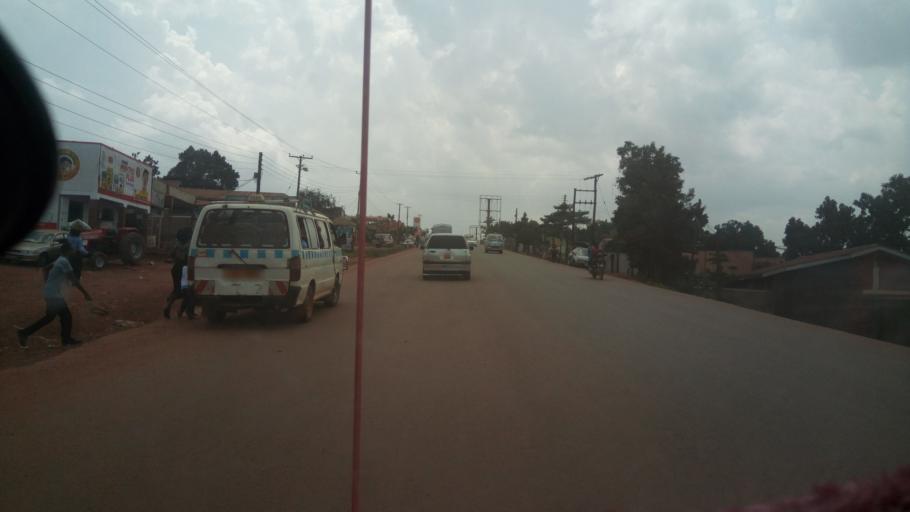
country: UG
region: Central Region
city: Kampala Central Division
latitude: 0.3538
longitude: 32.5360
